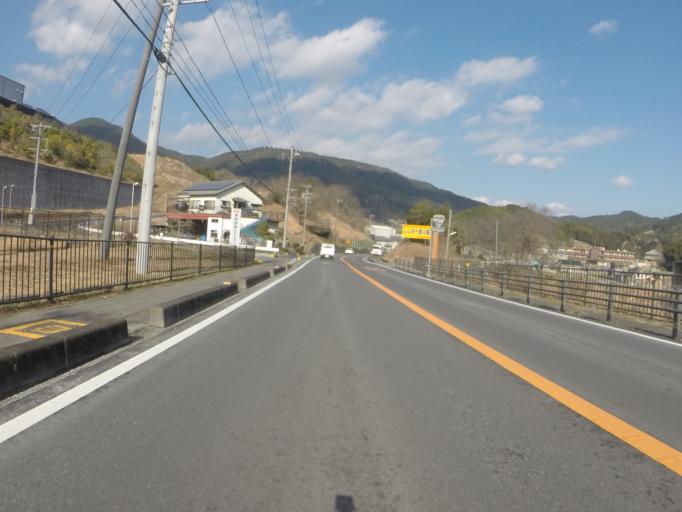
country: JP
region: Shizuoka
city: Fujinomiya
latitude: 35.1567
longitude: 138.5196
